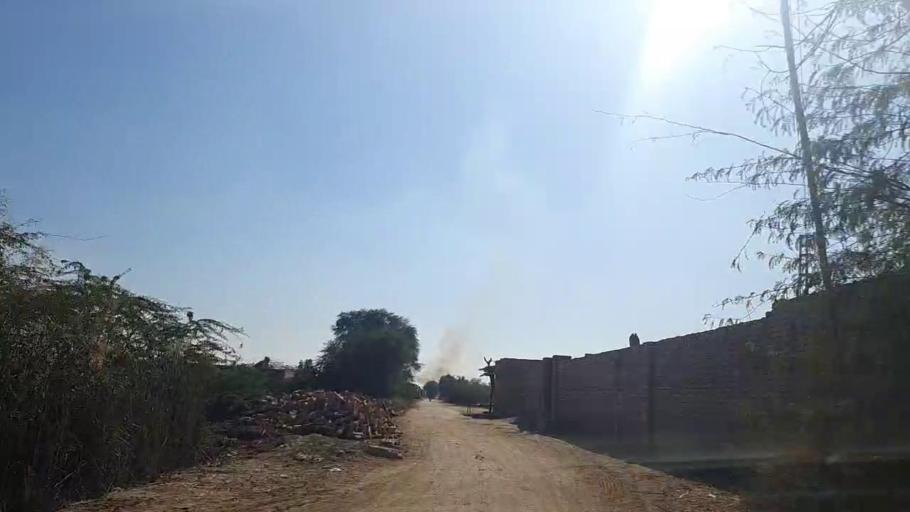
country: PK
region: Sindh
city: Sakrand
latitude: 26.2540
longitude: 68.1925
